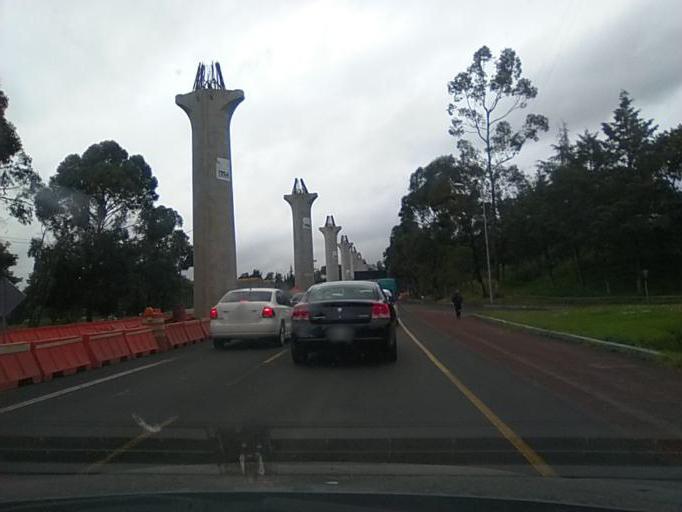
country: MX
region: Mexico City
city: Tlalpan
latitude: 19.2558
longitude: -99.1592
